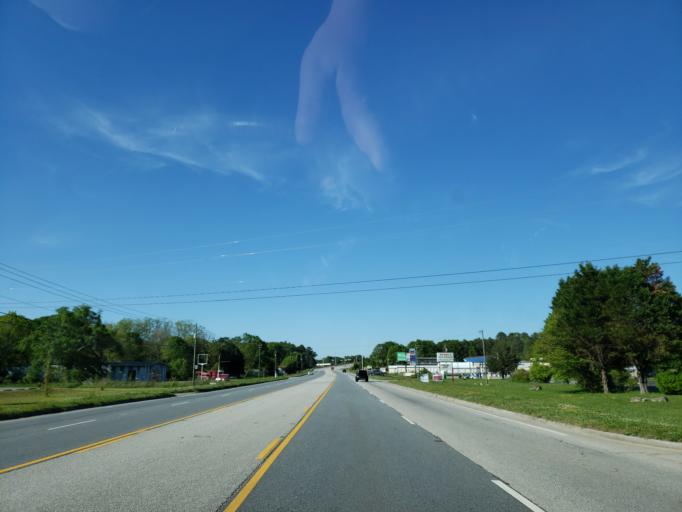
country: US
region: Georgia
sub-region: Polk County
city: Cedartown
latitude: 33.9830
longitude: -85.2560
